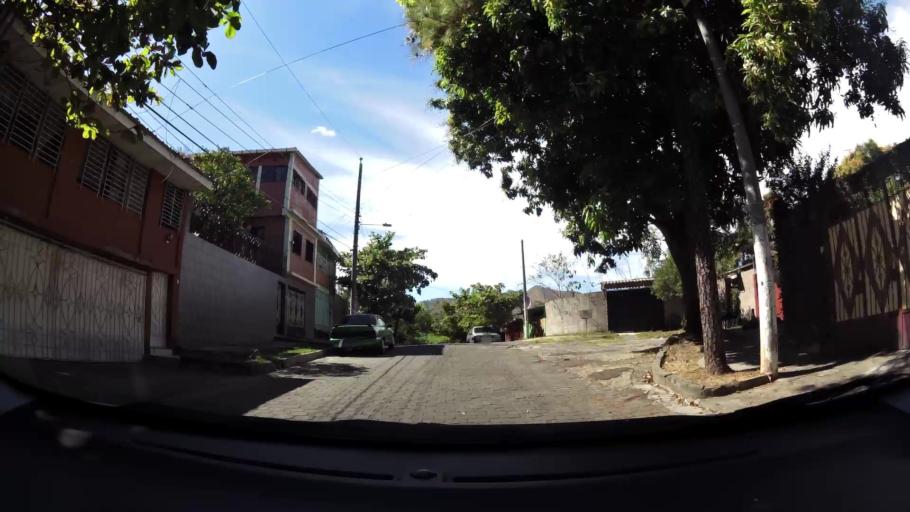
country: SV
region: San Salvador
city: Apopa
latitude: 13.8097
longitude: -89.1772
